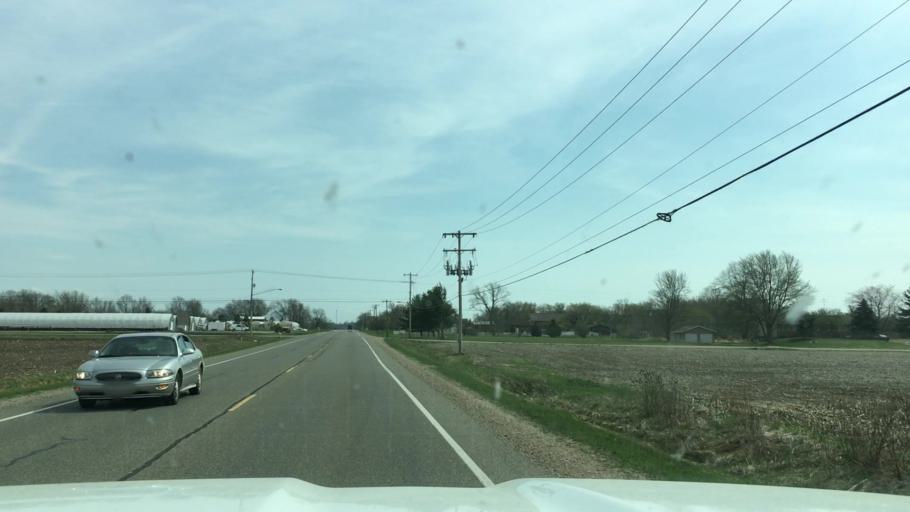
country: US
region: Michigan
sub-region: Ottawa County
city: Hudsonville
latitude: 42.8719
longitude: -85.9011
